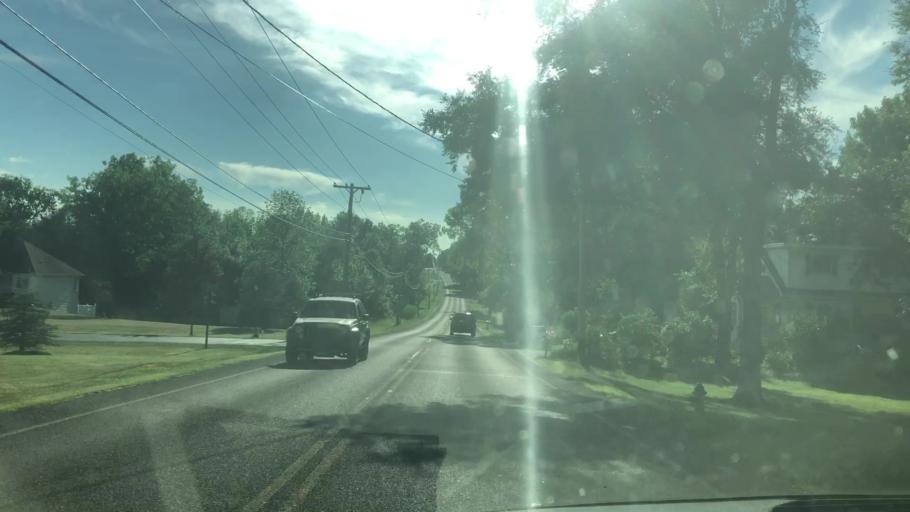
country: US
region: New York
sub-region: Wayne County
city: Macedon
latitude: 43.0441
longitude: -77.3512
